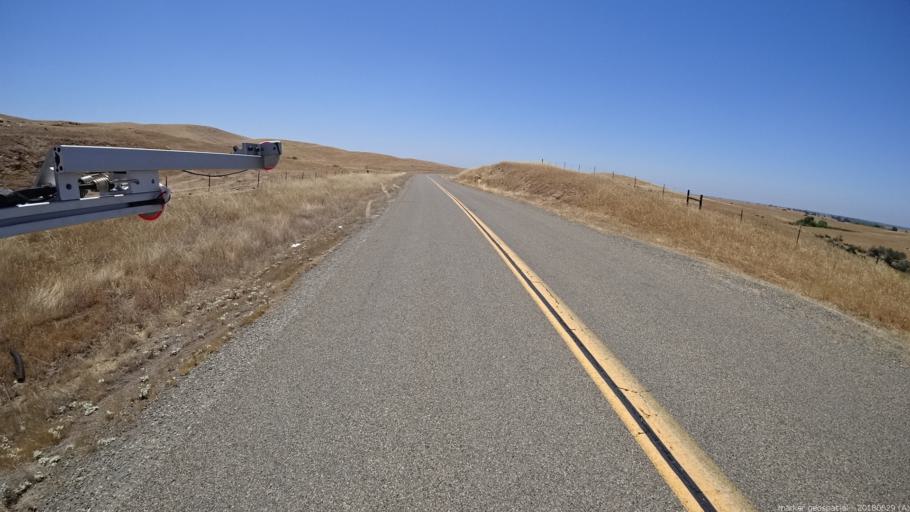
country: US
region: California
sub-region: Madera County
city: Bonadelle Ranchos-Madera Ranchos
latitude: 37.0908
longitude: -119.8813
